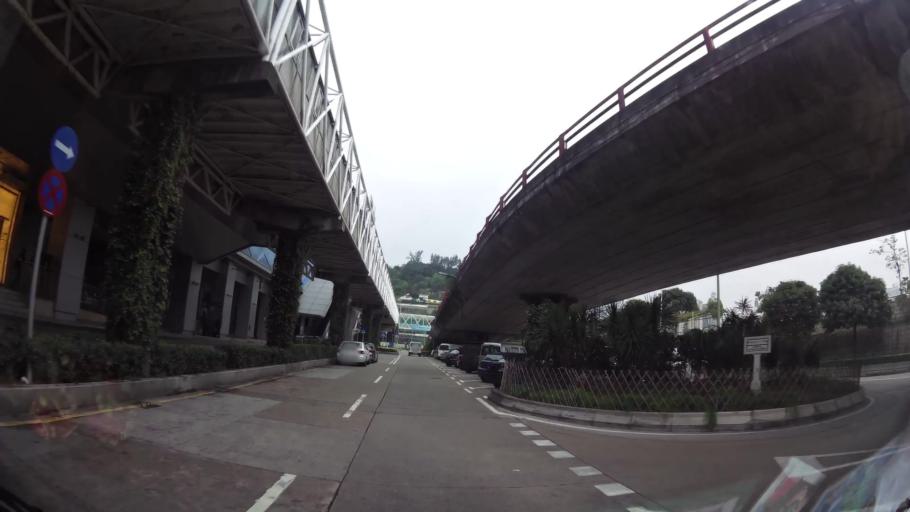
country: MO
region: Macau
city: Macau
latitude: 22.1972
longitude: 113.5562
